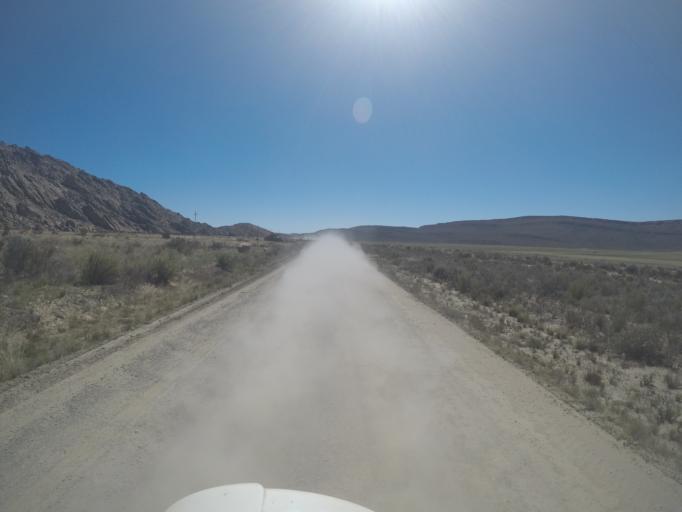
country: ZA
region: Western Cape
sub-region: Cape Winelands District Municipality
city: Ceres
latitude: -32.8406
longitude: 19.4495
